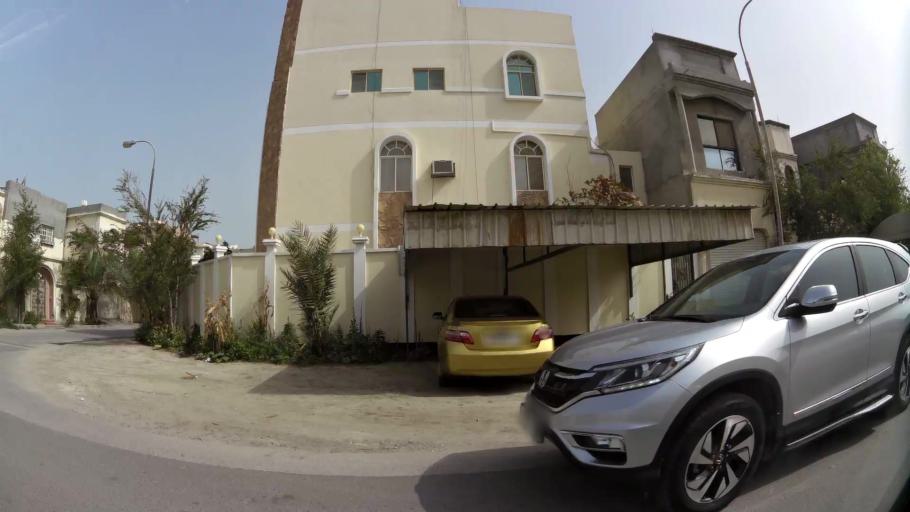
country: BH
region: Manama
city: Jidd Hafs
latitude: 26.2324
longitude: 50.5273
